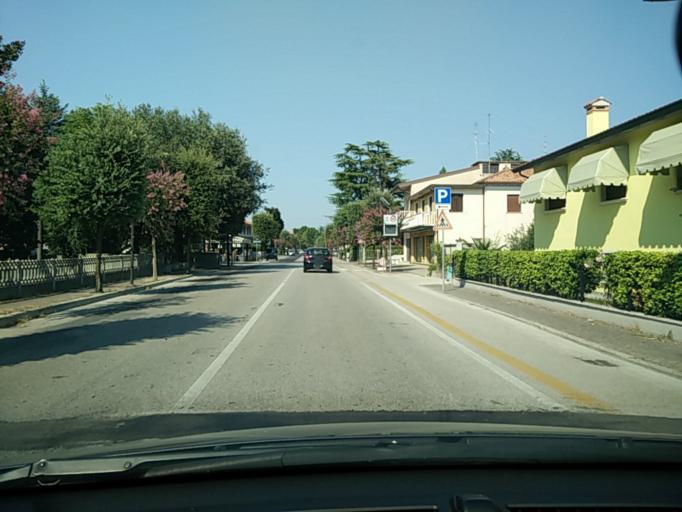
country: IT
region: Veneto
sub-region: Provincia di Venezia
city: San Giorgio di Livenza
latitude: 45.6499
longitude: 12.7960
